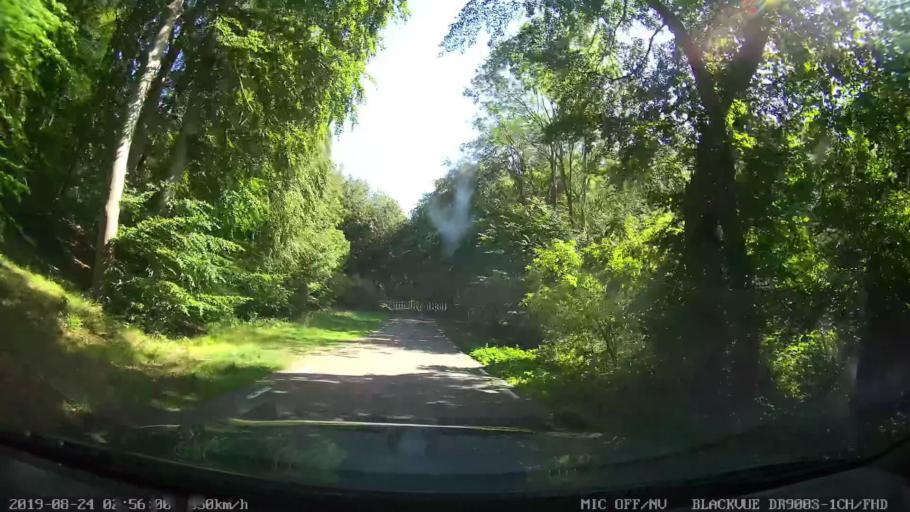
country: SE
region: Skane
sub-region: Trelleborgs Kommun
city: Anderslov
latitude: 55.4921
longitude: 13.3908
